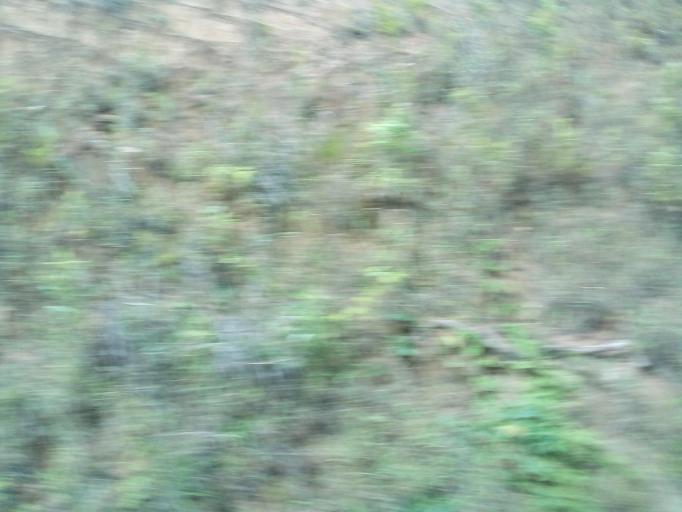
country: BR
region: Minas Gerais
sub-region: Caete
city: Caete
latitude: -19.9027
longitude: -43.7252
